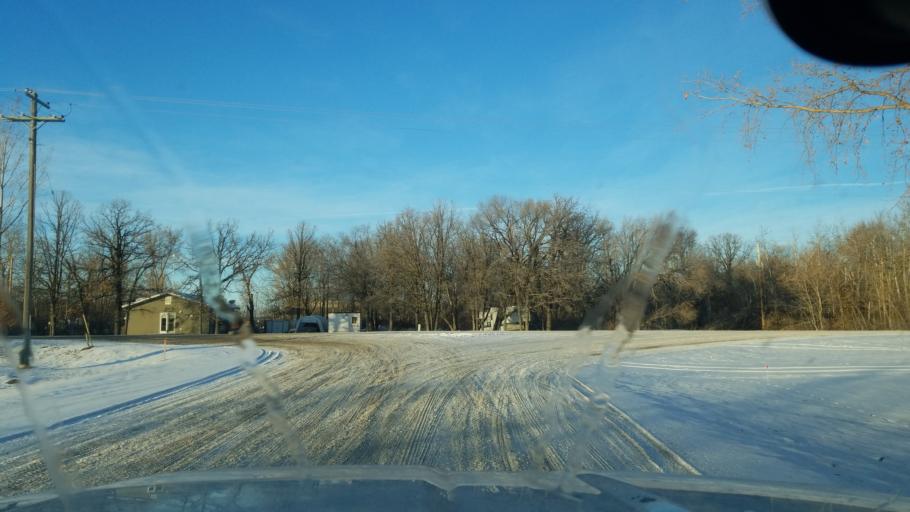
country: CA
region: Manitoba
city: Portage la Prairie
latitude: 49.9451
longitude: -98.3459
